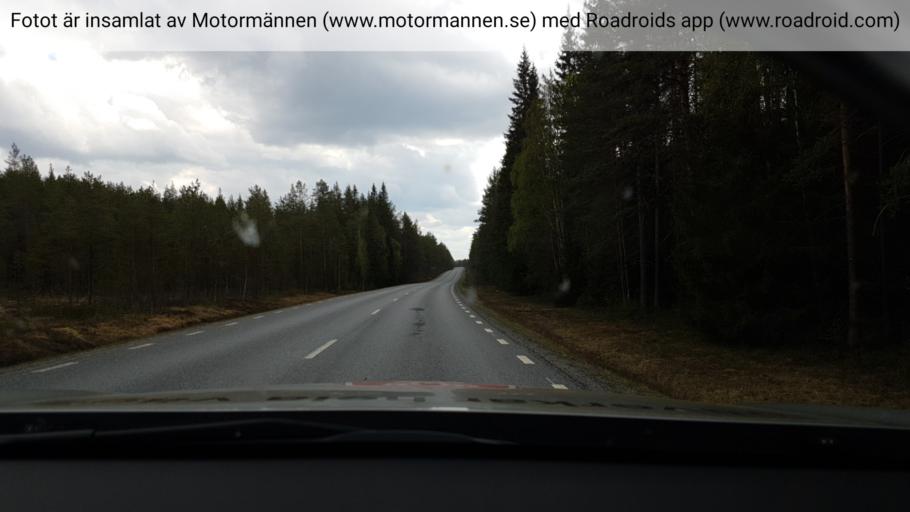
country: SE
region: Vaesterbotten
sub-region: Bjurholms Kommun
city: Bjurholm
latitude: 63.9837
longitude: 18.8074
